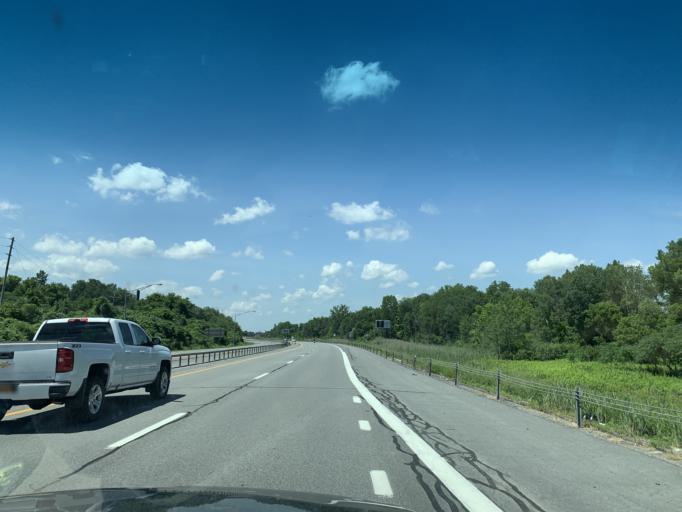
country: US
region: New York
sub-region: Oneida County
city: Utica
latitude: 43.0971
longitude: -75.1950
